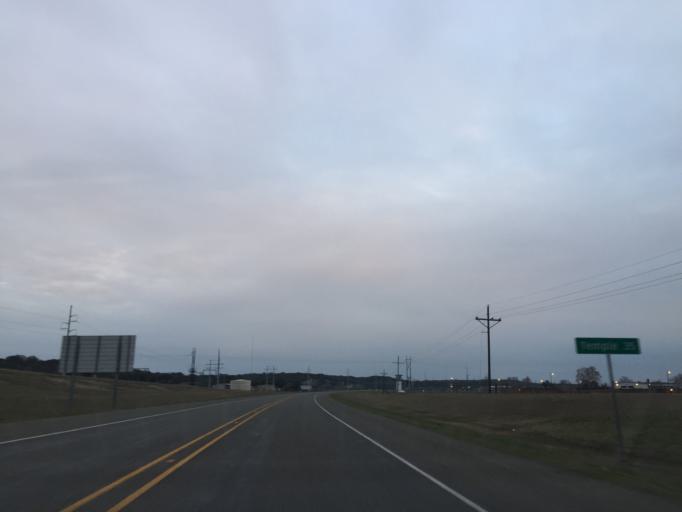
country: US
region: Texas
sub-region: Coryell County
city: Gatesville
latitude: 31.4774
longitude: -97.7239
